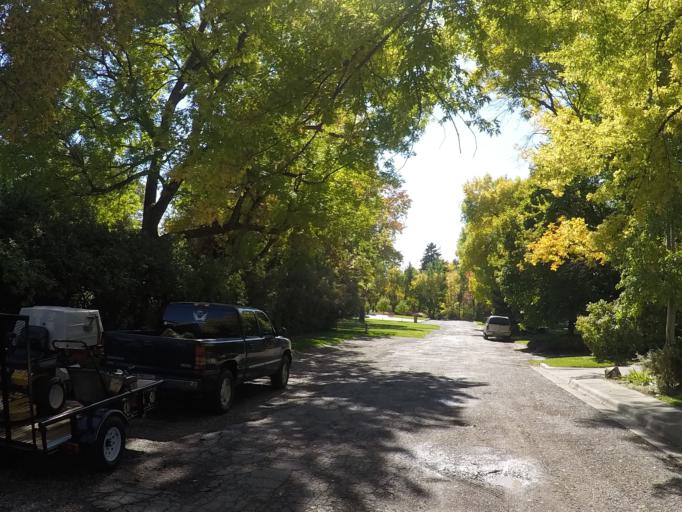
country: US
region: Montana
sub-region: Yellowstone County
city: Billings
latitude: 45.7965
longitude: -108.5323
